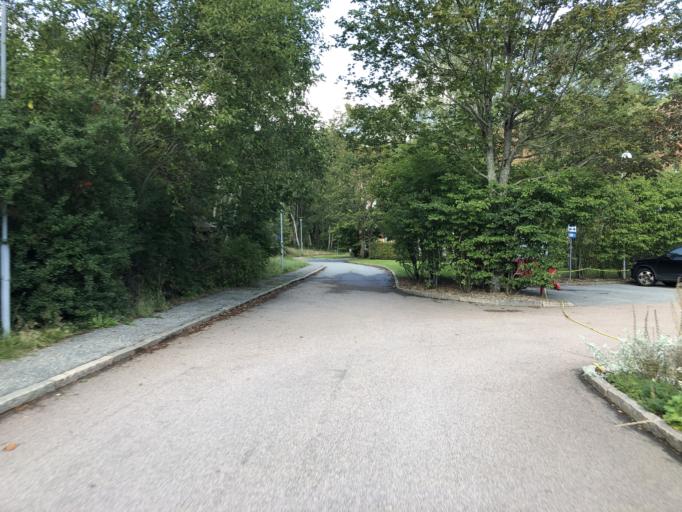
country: SE
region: Vaestra Goetaland
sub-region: Goteborg
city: Majorna
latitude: 57.7314
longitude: 11.9028
